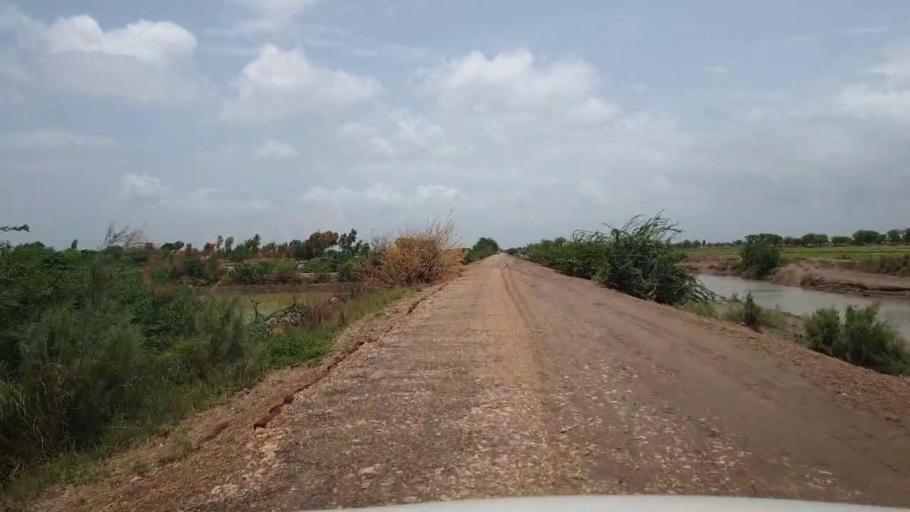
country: PK
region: Sindh
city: Kario
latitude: 24.7092
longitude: 68.6025
